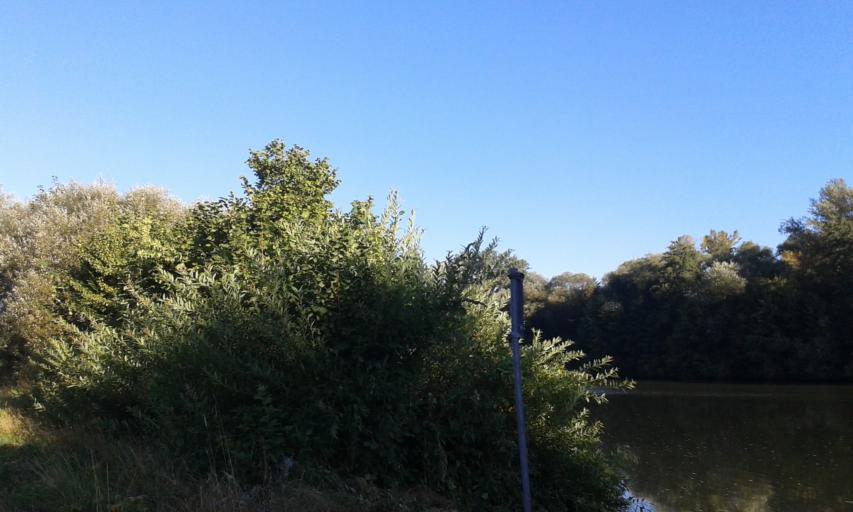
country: DE
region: Bavaria
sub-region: Upper Franconia
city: Bischberg
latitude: 49.9147
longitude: 10.8260
